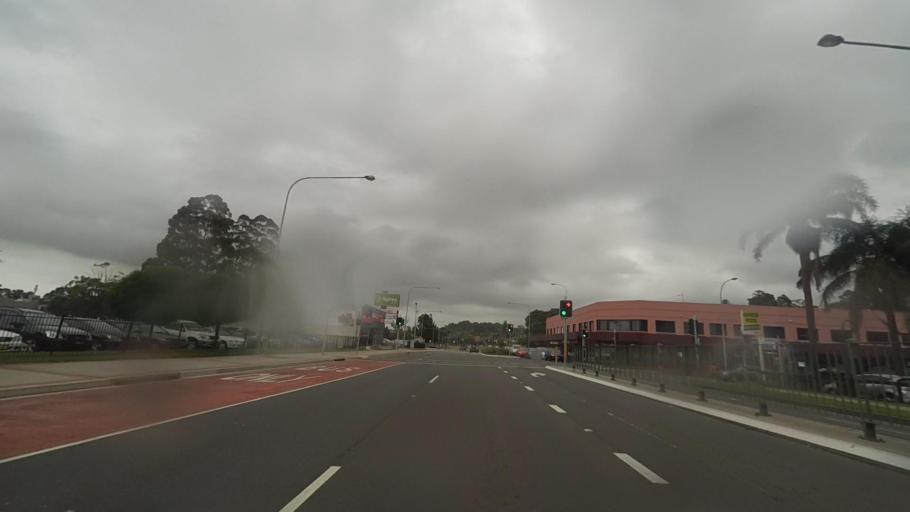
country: AU
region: New South Wales
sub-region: Wollongong
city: Mangerton
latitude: -34.4349
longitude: 150.8623
